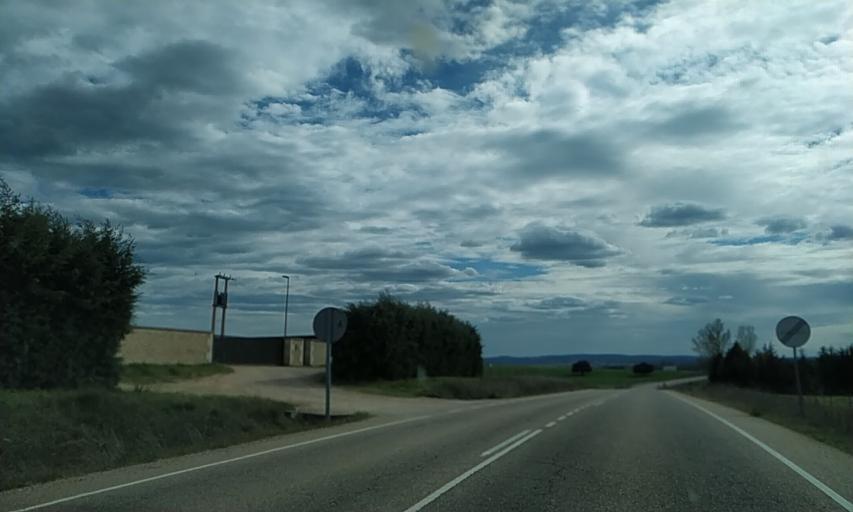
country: ES
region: Castille and Leon
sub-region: Provincia de Salamanca
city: Ciudad Rodrigo
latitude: 40.5683
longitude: -6.5465
